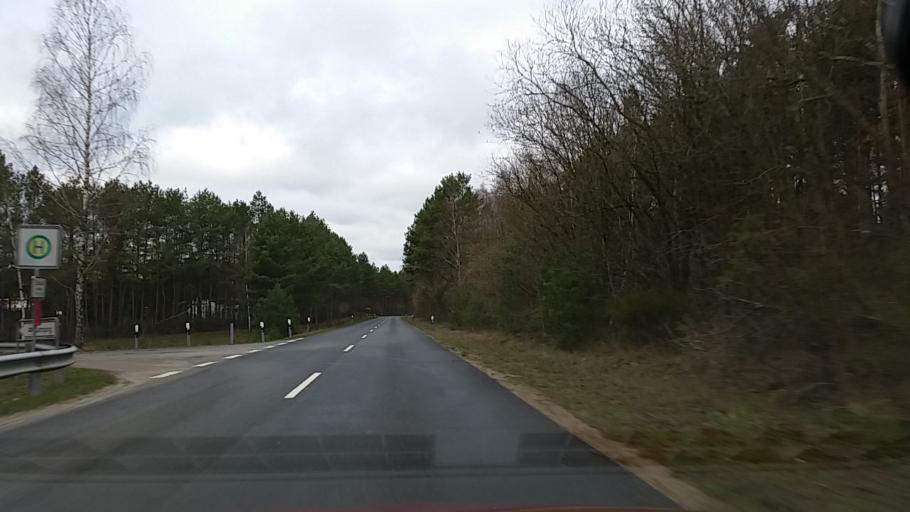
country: DE
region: Lower Saxony
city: Bodenteich
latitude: 52.8462
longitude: 10.6627
